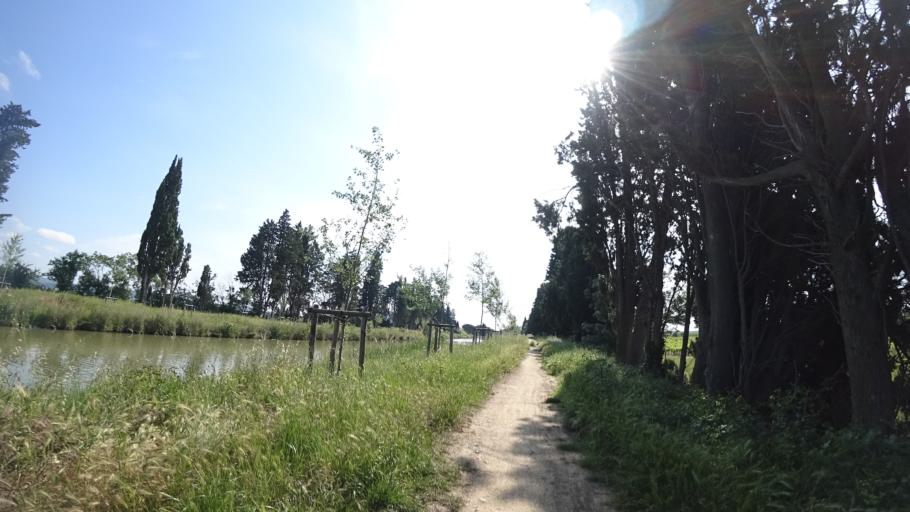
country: FR
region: Languedoc-Roussillon
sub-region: Departement de l'Herault
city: Olonzac
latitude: 43.2696
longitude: 2.7264
